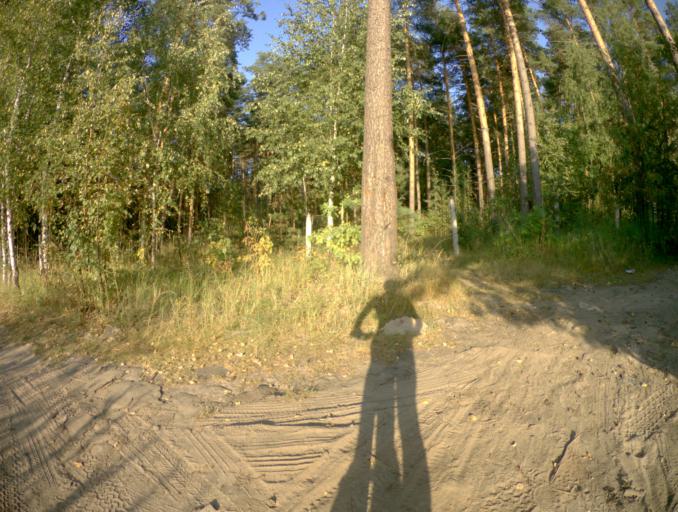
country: RU
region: Vladimir
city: Kommunar
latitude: 56.0502
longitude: 40.4491
